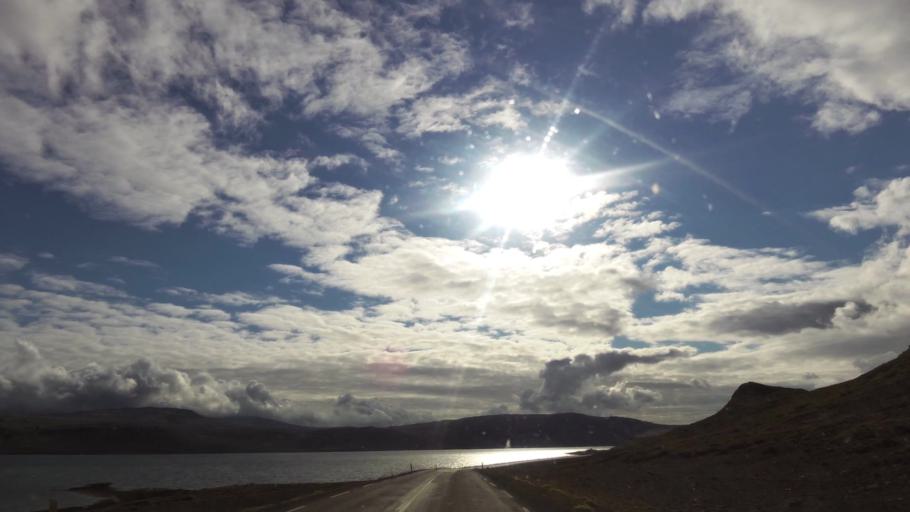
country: IS
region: West
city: Olafsvik
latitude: 65.5384
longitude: -23.8502
